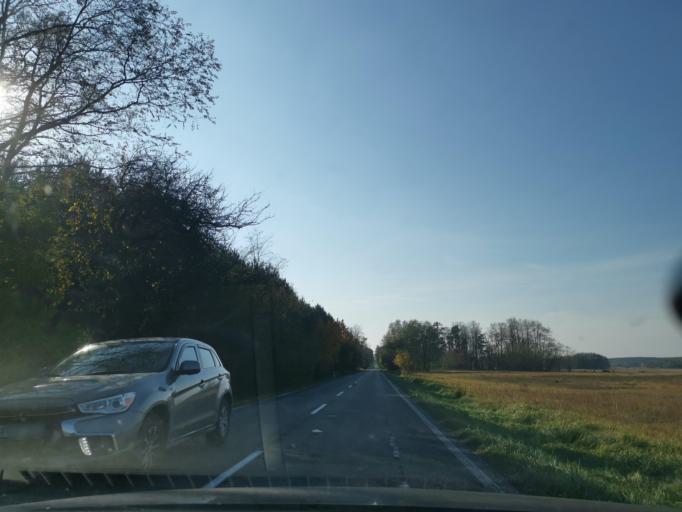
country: SK
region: Trnavsky
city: Gbely
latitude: 48.5719
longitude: 17.1611
